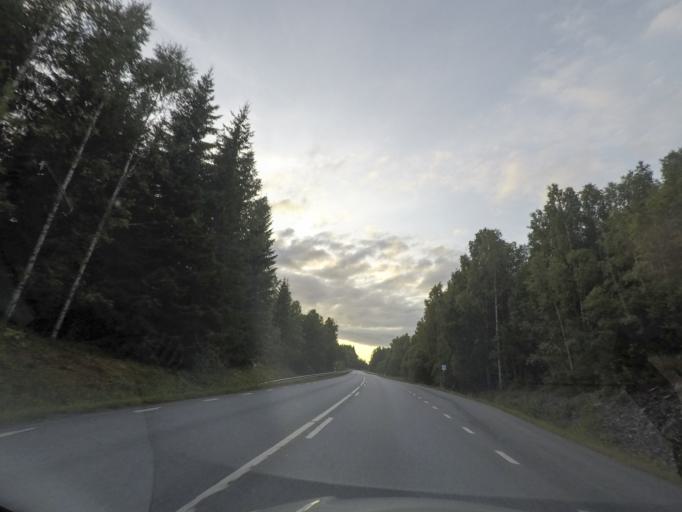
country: SE
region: OErebro
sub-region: Hallefors Kommun
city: Haellefors
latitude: 59.6622
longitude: 14.5695
